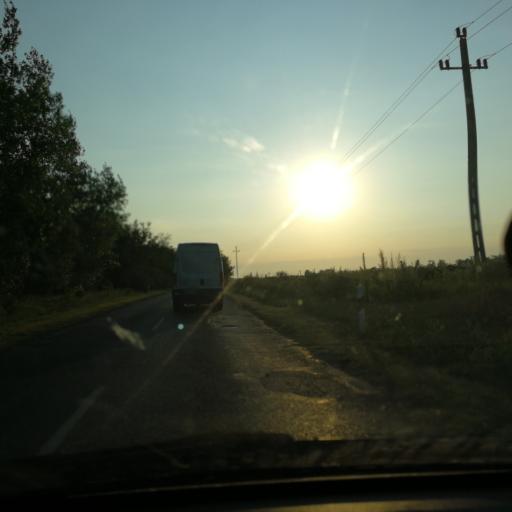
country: HU
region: Bacs-Kiskun
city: Kiskunhalas
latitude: 46.4422
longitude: 19.5844
